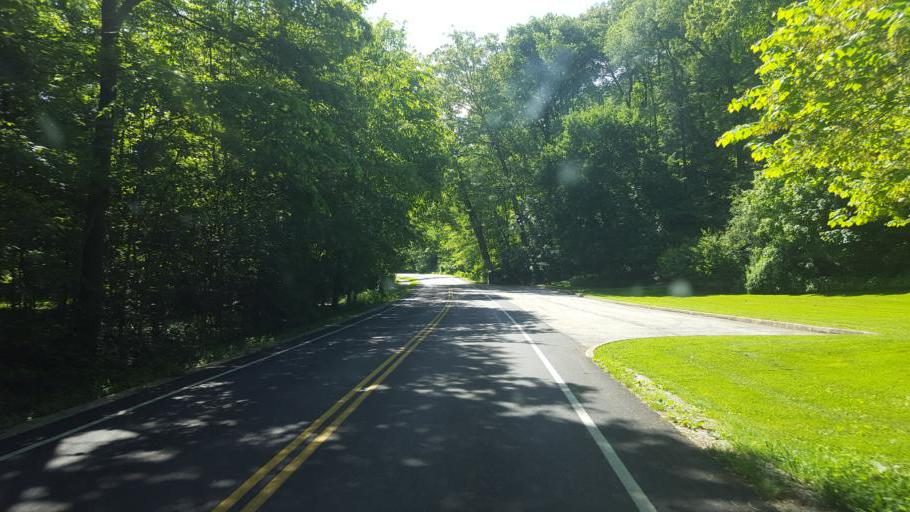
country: US
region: Ohio
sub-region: Summit County
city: Fairlawn
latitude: 41.1305
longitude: -81.5569
